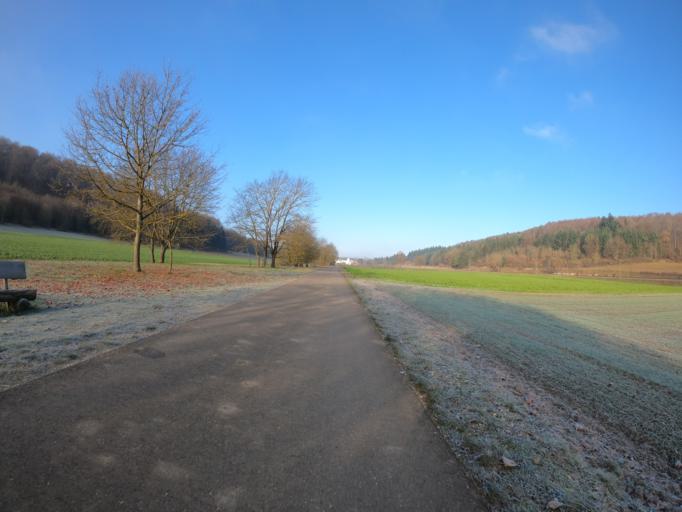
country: DE
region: Baden-Wuerttemberg
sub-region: Tuebingen Region
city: Amstetten
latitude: 48.5630
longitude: 9.8878
